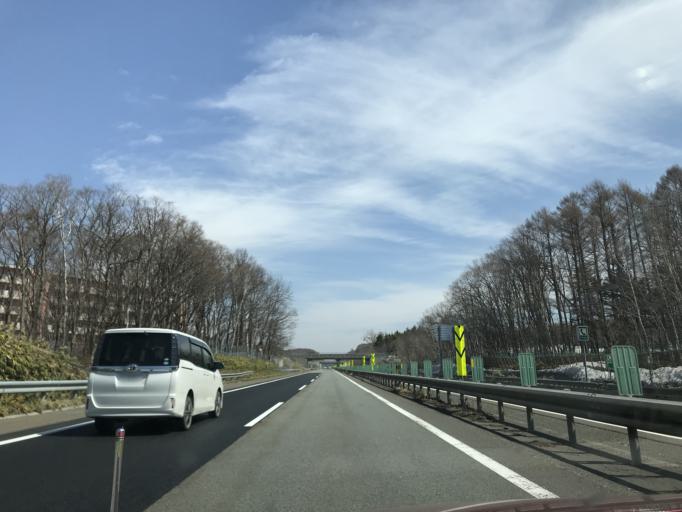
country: JP
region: Hokkaido
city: Iwamizawa
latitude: 43.1787
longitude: 141.7736
